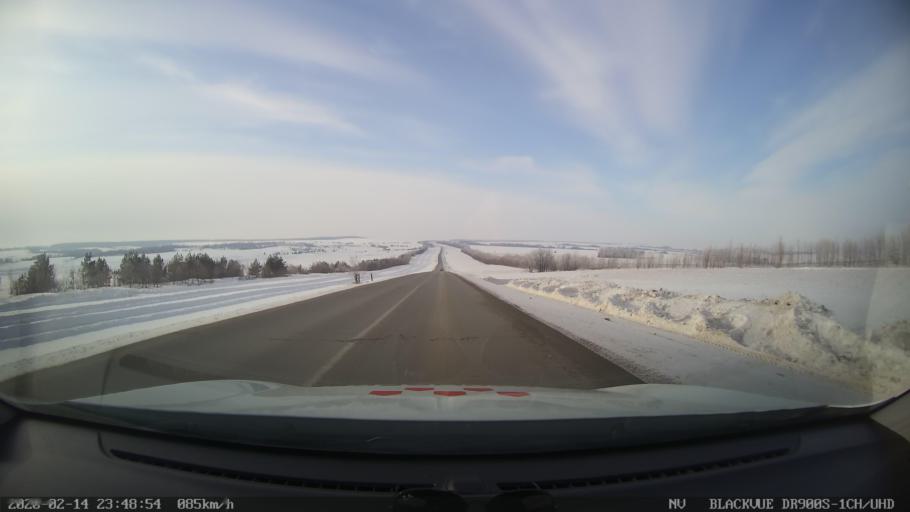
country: RU
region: Tatarstan
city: Kuybyshevskiy Zaton
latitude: 55.2502
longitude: 49.1939
